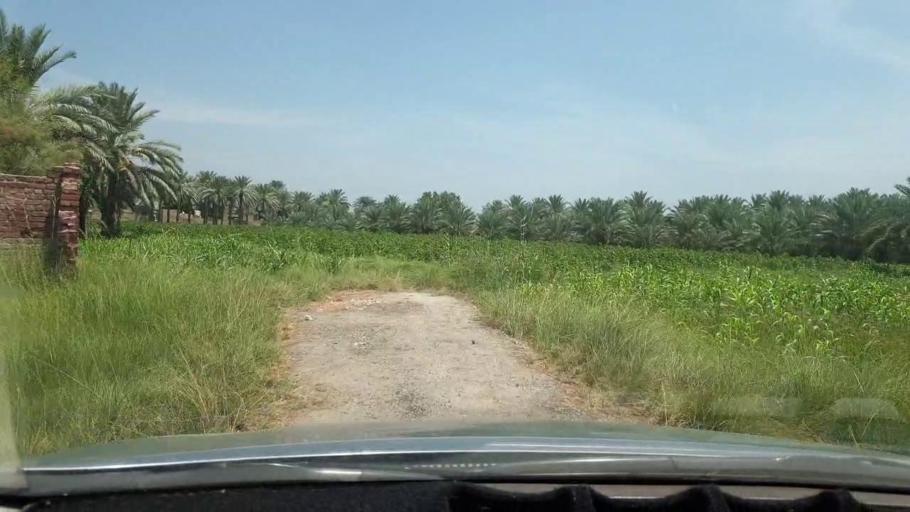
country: PK
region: Sindh
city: Khairpur
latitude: 27.4925
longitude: 68.7691
